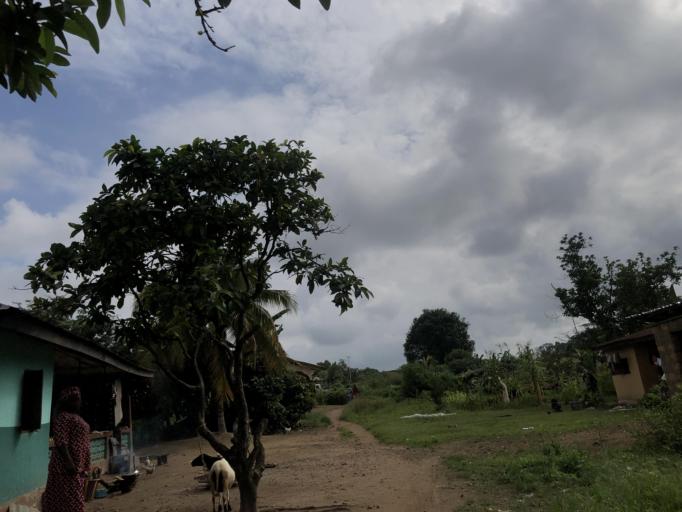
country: SL
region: Eastern Province
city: Kailahun
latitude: 8.2750
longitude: -10.5650
